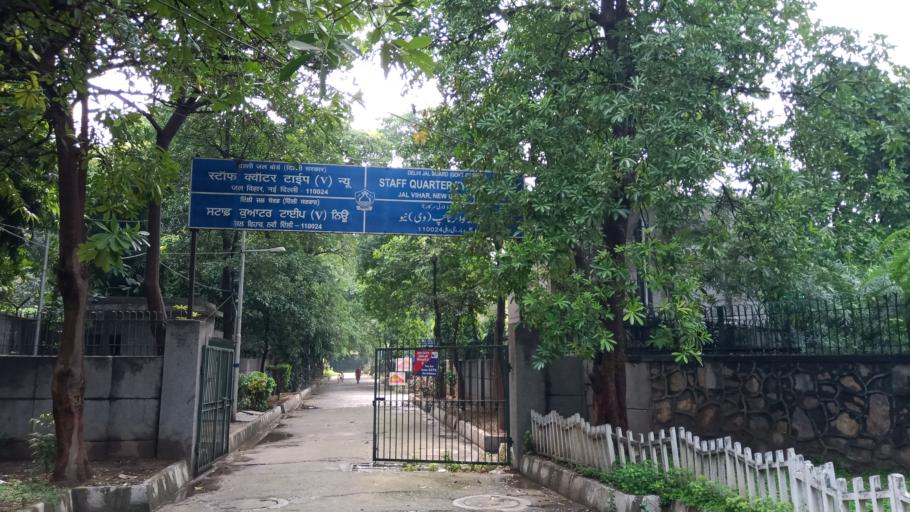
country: IN
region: NCT
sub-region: New Delhi
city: New Delhi
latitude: 28.5771
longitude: 77.2472
